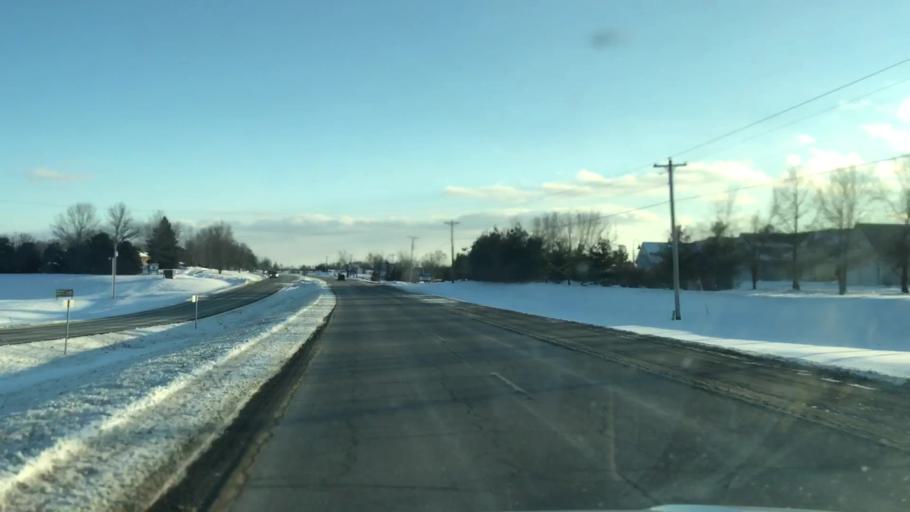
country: US
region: Missouri
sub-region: Andrew County
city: Country Club Village
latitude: 39.8769
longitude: -94.8092
